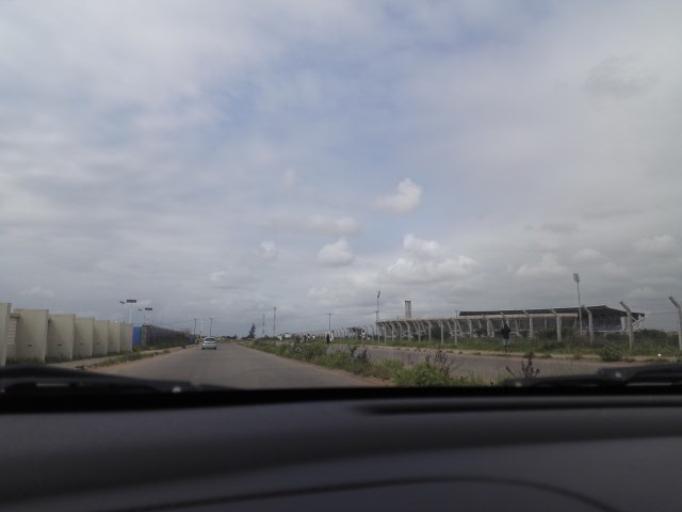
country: MZ
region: Maputo City
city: Maputo
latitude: -25.8246
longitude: 32.5805
